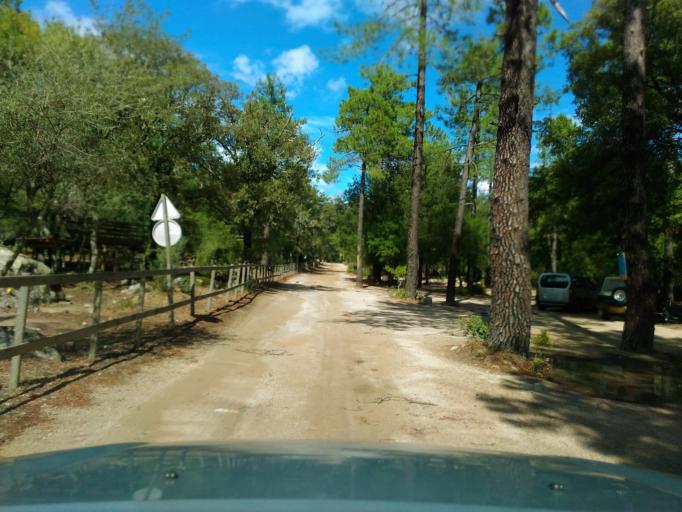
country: FR
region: Corsica
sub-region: Departement de la Corse-du-Sud
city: Porto-Vecchio
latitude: 41.7199
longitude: 9.3012
